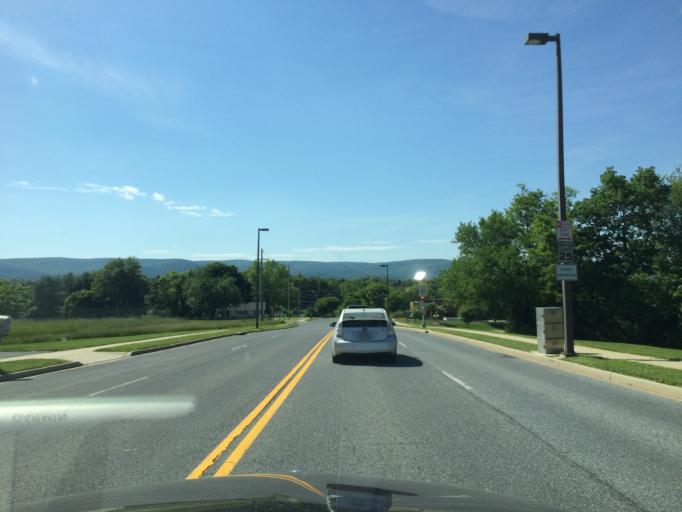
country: US
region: Maryland
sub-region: Frederick County
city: Clover Hill
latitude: 39.4558
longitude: -77.4076
